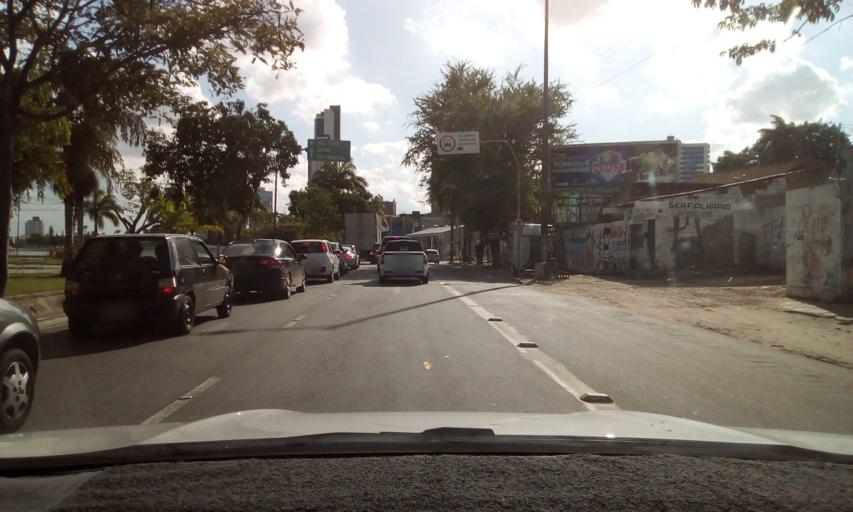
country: BR
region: Paraiba
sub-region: Campina Grande
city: Campina Grande
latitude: -7.2224
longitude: -35.8766
